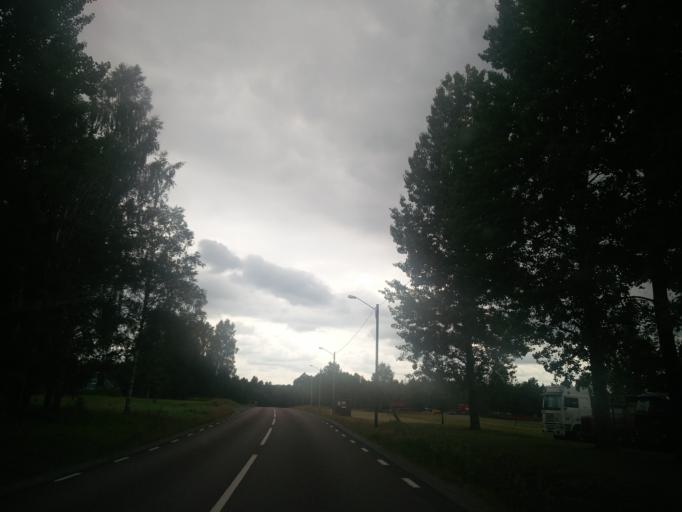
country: SE
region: Vaermland
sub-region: Arvika Kommun
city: Arvika
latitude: 59.8860
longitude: 12.6271
